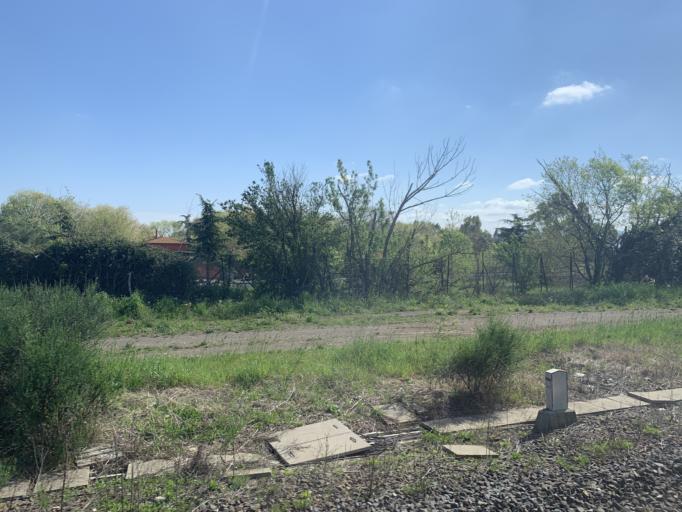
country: IT
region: Latium
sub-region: Citta metropolitana di Roma Capitale
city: Ciampino
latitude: 41.8291
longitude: 12.5701
